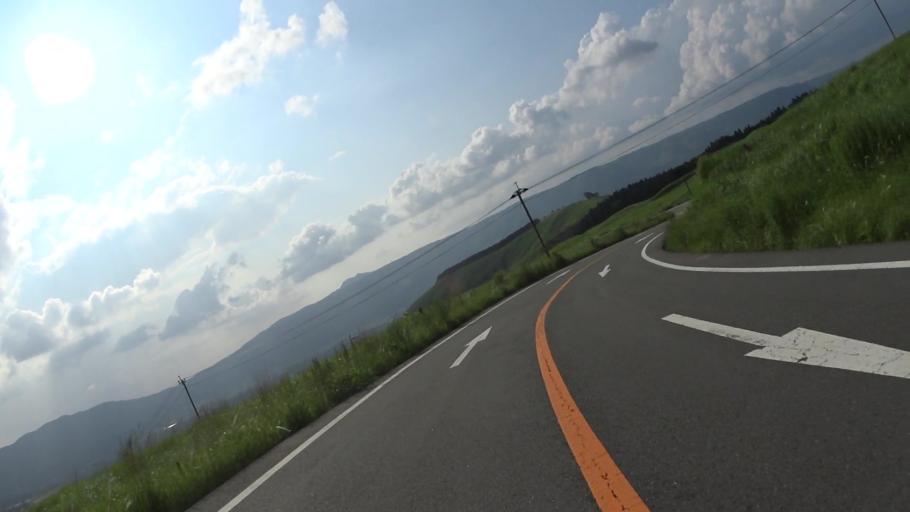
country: JP
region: Kumamoto
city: Aso
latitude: 32.9028
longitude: 131.0328
